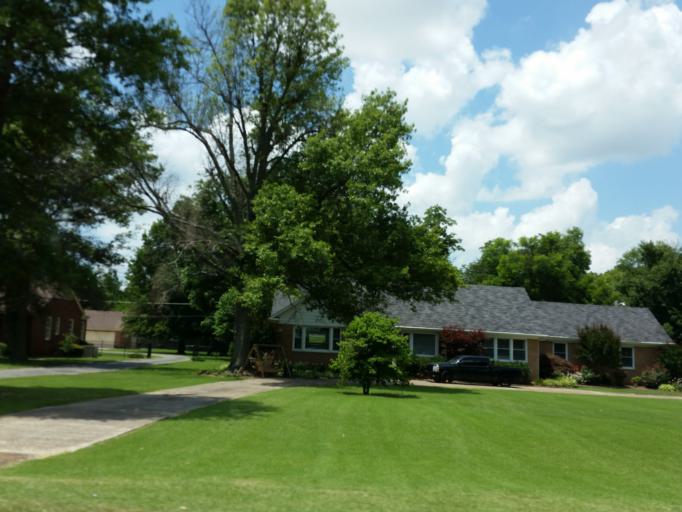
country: US
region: Tennessee
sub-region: Lake County
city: Ridgely
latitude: 36.2685
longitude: -89.4781
